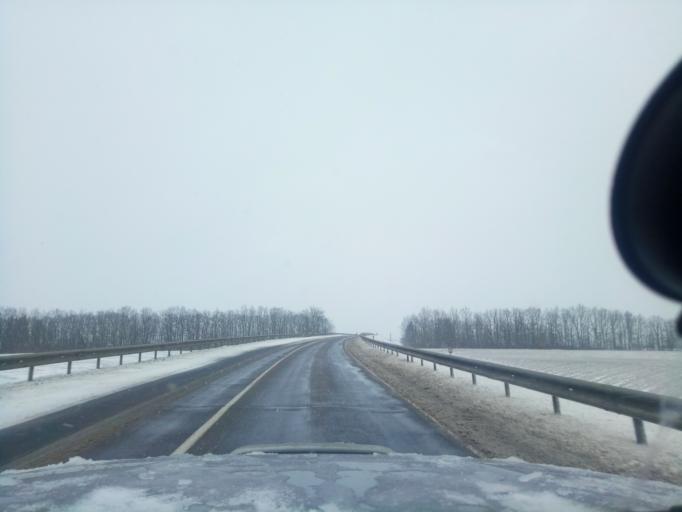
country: BY
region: Minsk
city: Haradzyeya
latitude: 53.3318
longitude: 26.5454
